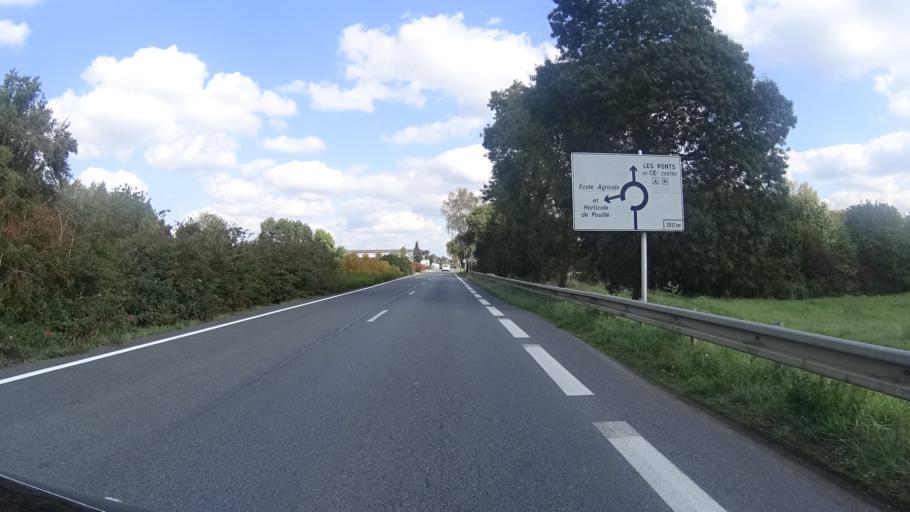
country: FR
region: Pays de la Loire
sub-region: Departement de Maine-et-Loire
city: Les Ponts-de-Ce
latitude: 47.4308
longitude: -0.5384
